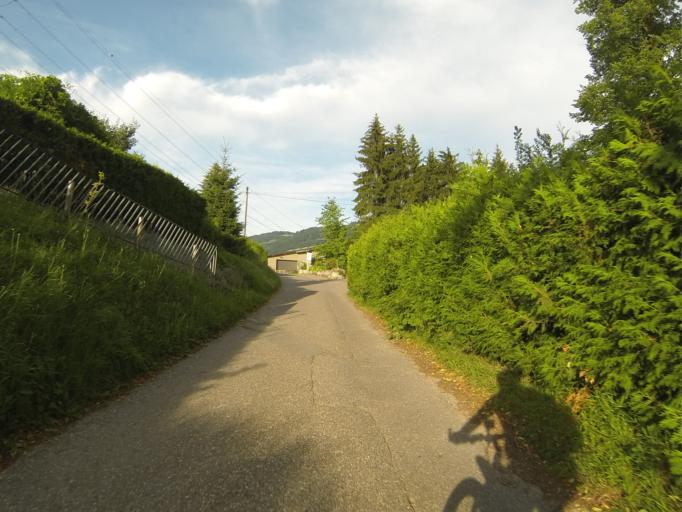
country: CH
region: Lucerne
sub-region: Lucerne-Land District
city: Buchrain
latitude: 47.1015
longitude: 8.3635
